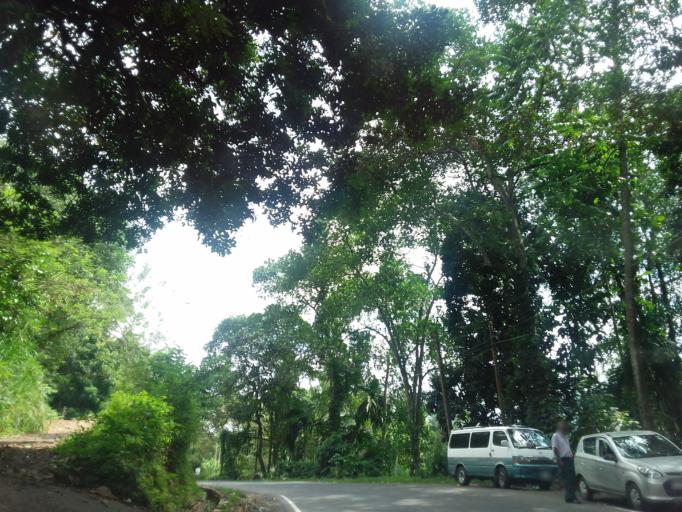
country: LK
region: Central
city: Hatton
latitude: 6.9978
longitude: 80.4006
